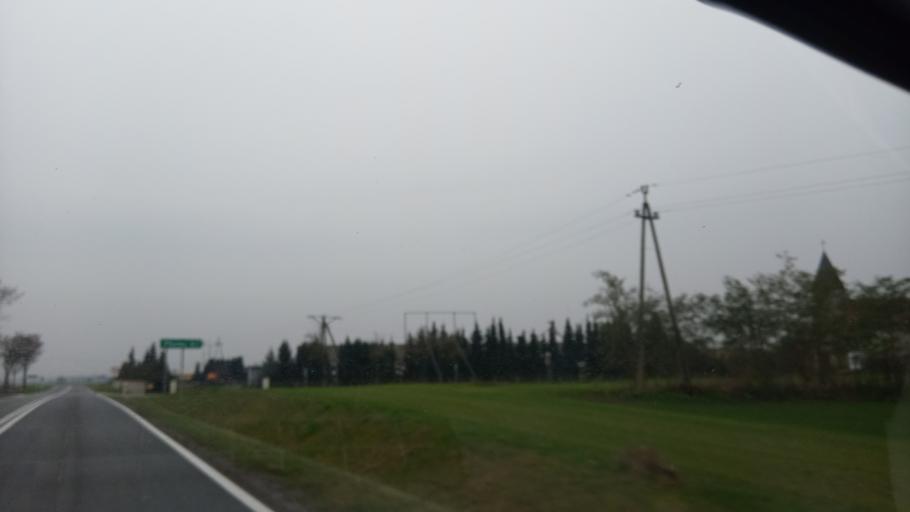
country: PL
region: Kujawsko-Pomorskie
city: Kamien Krajenski
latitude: 53.5026
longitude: 17.5072
